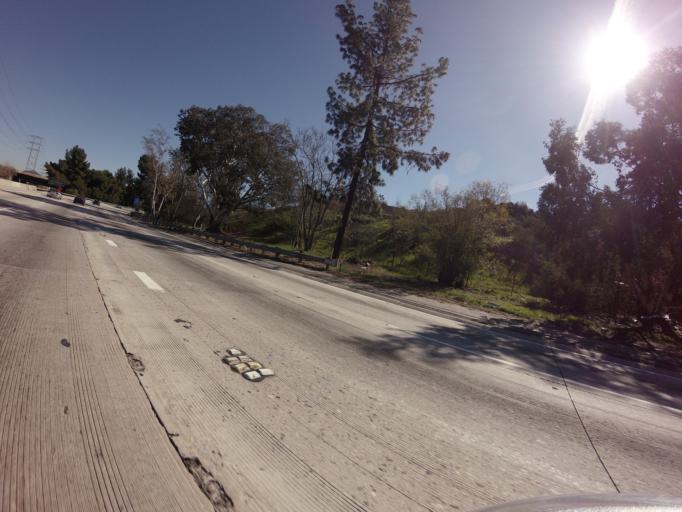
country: US
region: California
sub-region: Los Angeles County
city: North Glendale
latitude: 34.1553
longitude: -118.2922
